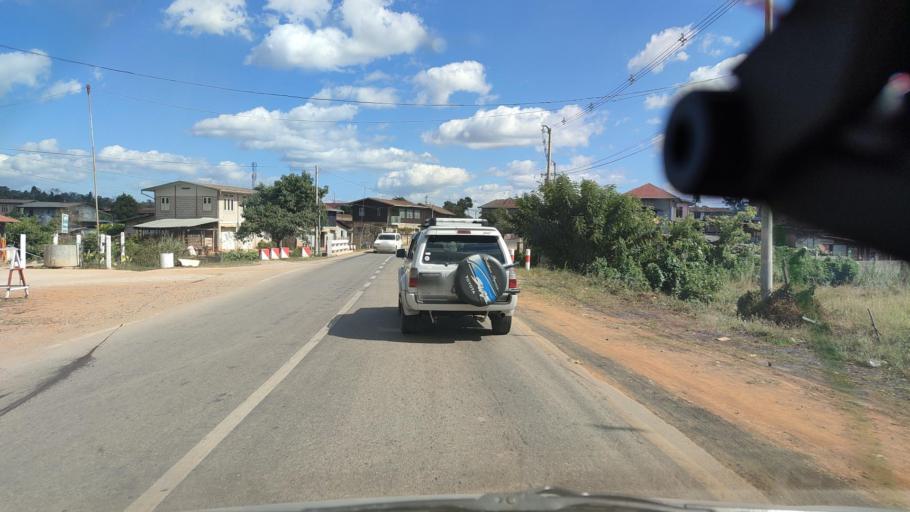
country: MM
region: Shan
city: Taunggyi
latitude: 20.9297
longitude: 97.5575
